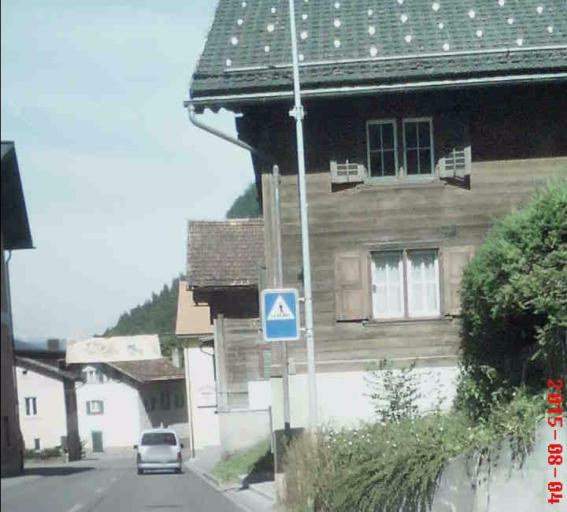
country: CH
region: Grisons
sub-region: Praettigau/Davos District
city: Klosters Serneus
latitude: 46.8822
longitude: 9.8789
